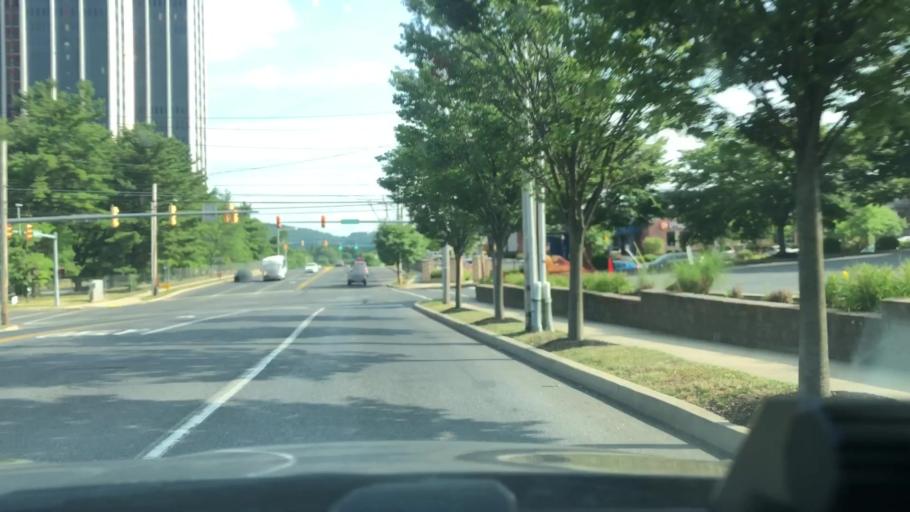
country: US
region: Pennsylvania
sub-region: Northampton County
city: Bethlehem
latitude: 40.6342
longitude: -75.3958
